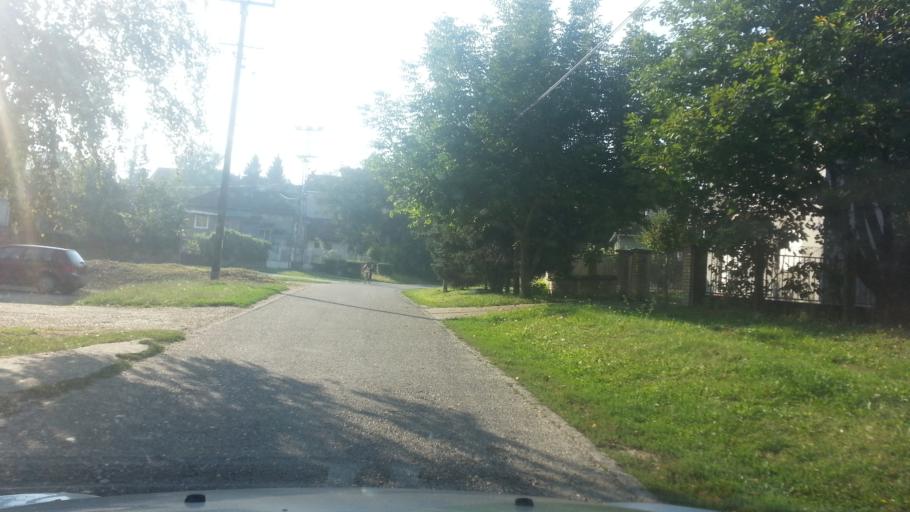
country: RS
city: Novi Banovci
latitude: 44.9530
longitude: 20.2874
